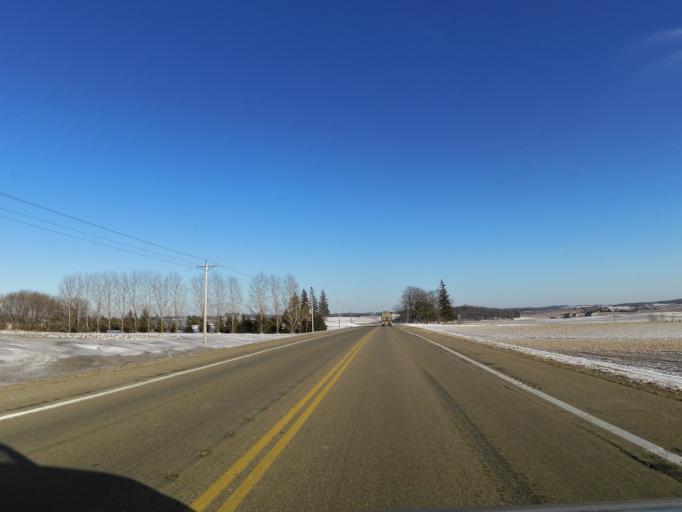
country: US
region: Minnesota
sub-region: Rice County
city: Lonsdale
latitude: 44.4860
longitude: -93.4969
